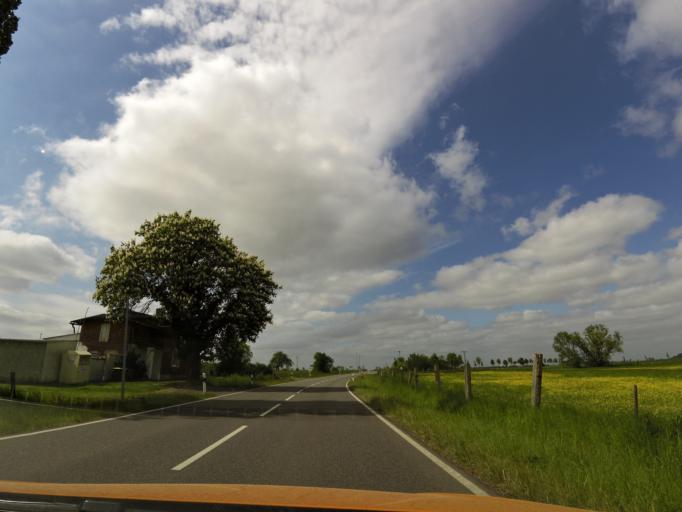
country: DE
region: Saxony-Anhalt
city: Loburg
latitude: 52.1242
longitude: 12.0192
